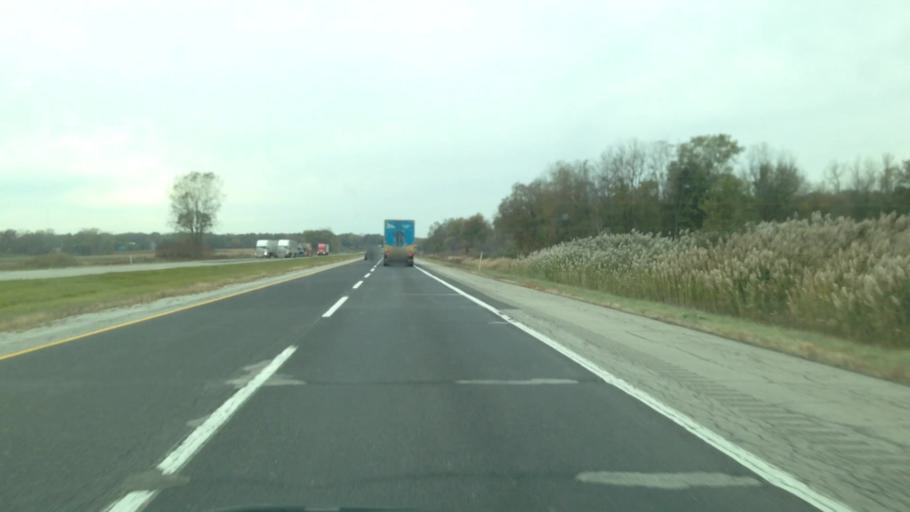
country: US
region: Indiana
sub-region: Steuben County
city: Fremont
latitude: 41.6880
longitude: -84.8909
